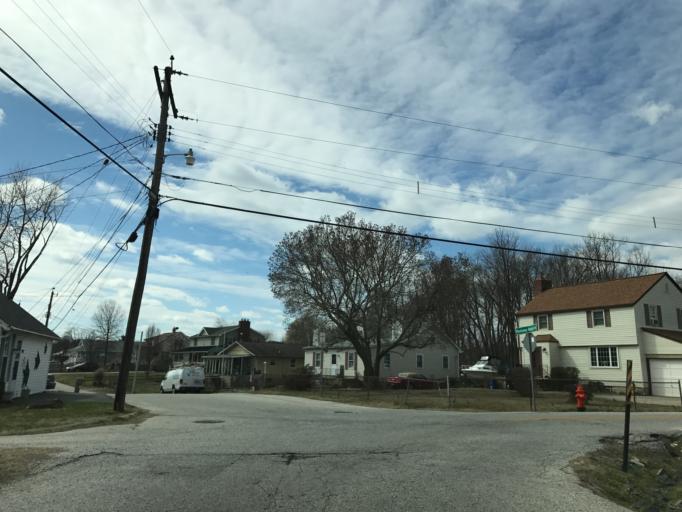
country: US
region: Maryland
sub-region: Baltimore County
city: Bowleys Quarters
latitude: 39.2919
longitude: -76.4004
